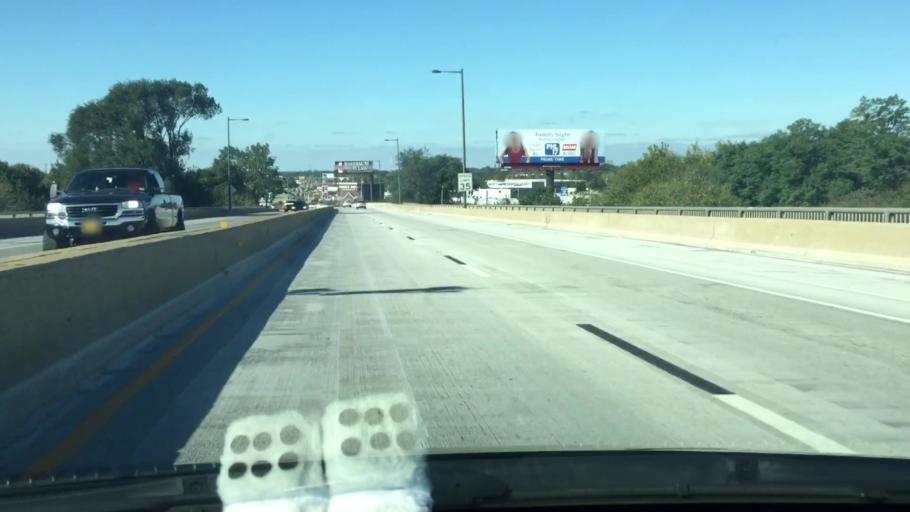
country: US
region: Pennsylvania
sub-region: Delaware County
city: Colwyn
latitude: 39.9194
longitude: -75.2044
